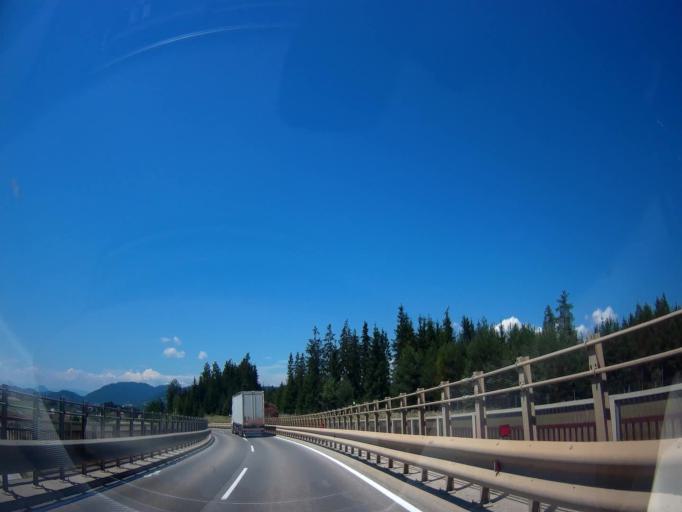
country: AT
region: Carinthia
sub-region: Politischer Bezirk Volkermarkt
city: Eberndorf
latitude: 46.6264
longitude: 14.6431
